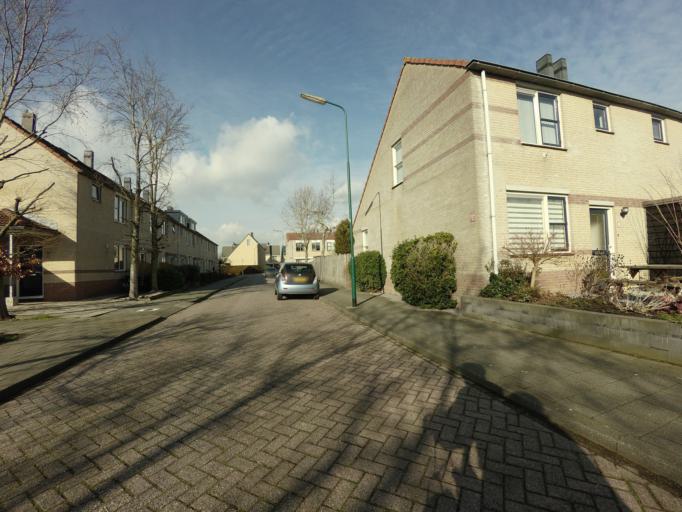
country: NL
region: Utrecht
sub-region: Gemeente Montfoort
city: Montfoort
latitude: 52.0665
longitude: 4.9193
